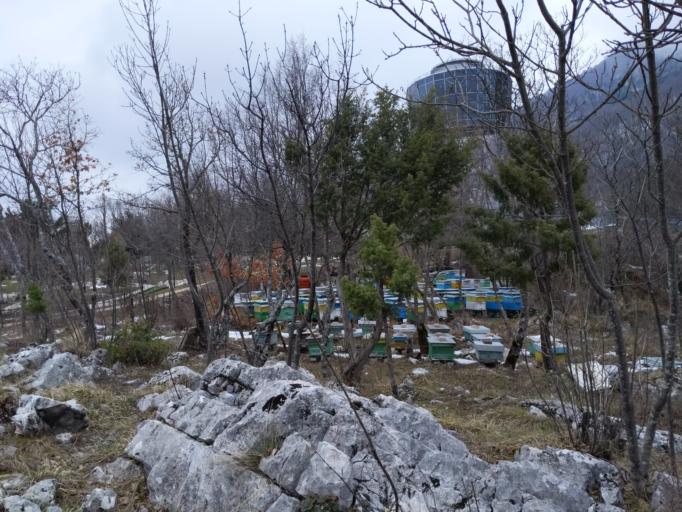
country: AL
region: Tirane
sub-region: Rrethi i Tiranes
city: Dajt
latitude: 41.3674
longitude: 19.9056
